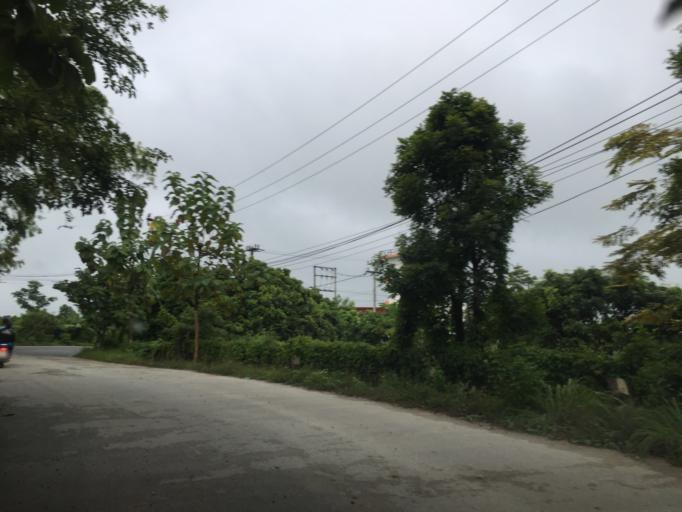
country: TH
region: Lamphun
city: Ban Thi
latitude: 18.6674
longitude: 99.0782
